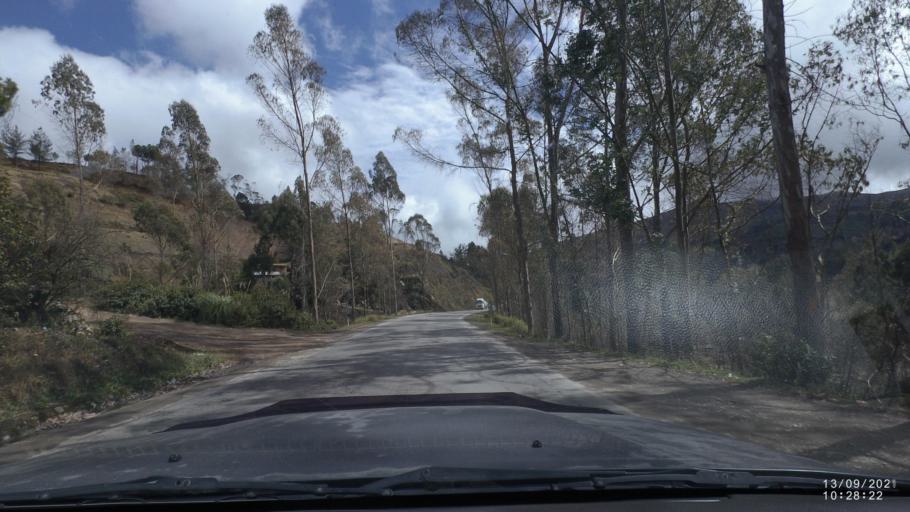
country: BO
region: Cochabamba
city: Colomi
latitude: -17.2804
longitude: -65.8742
